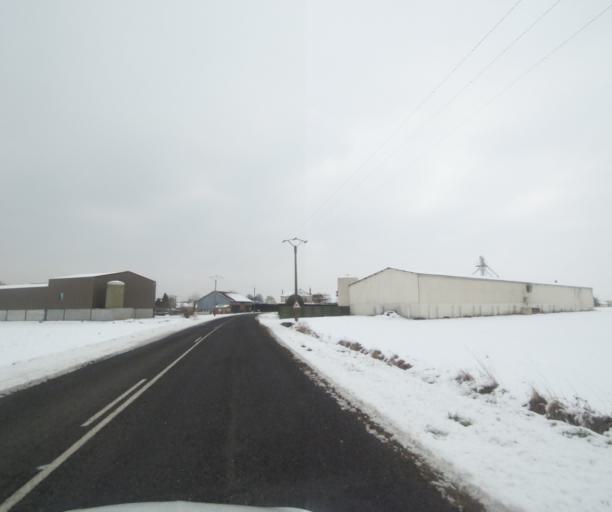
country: FR
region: Champagne-Ardenne
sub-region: Departement de la Haute-Marne
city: Saint-Dizier
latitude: 48.5830
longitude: 4.8943
